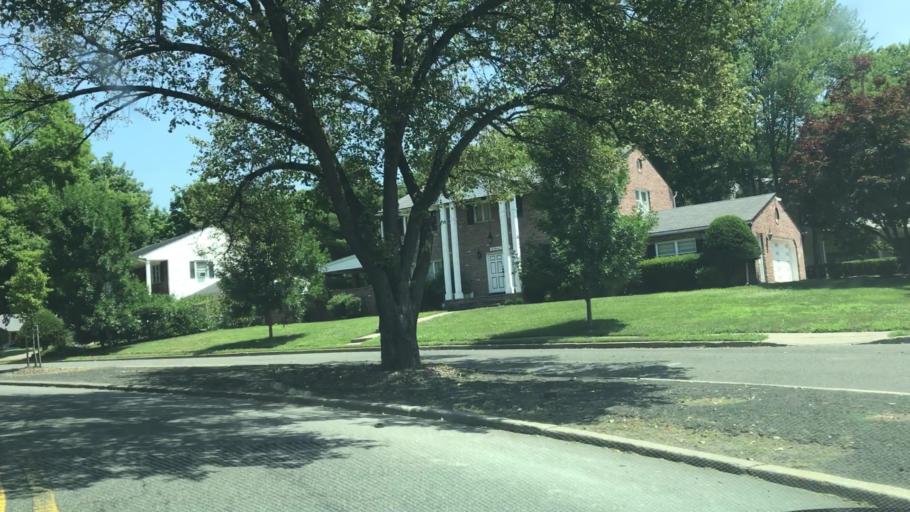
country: US
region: New Jersey
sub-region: Bergen County
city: River Edge
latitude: 40.9349
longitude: -74.0508
